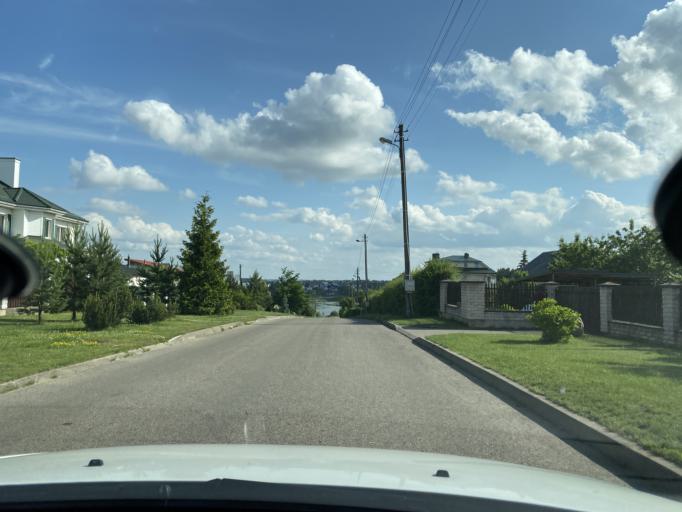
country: LT
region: Vilnius County
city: Pasilaiciai
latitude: 54.7384
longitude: 25.1983
